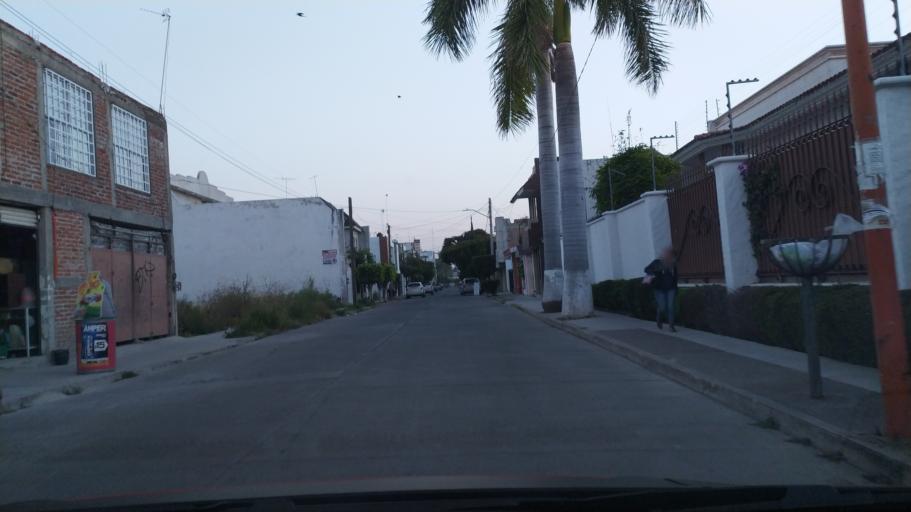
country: MX
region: Guanajuato
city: San Francisco del Rincon
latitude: 21.0130
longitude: -101.8614
